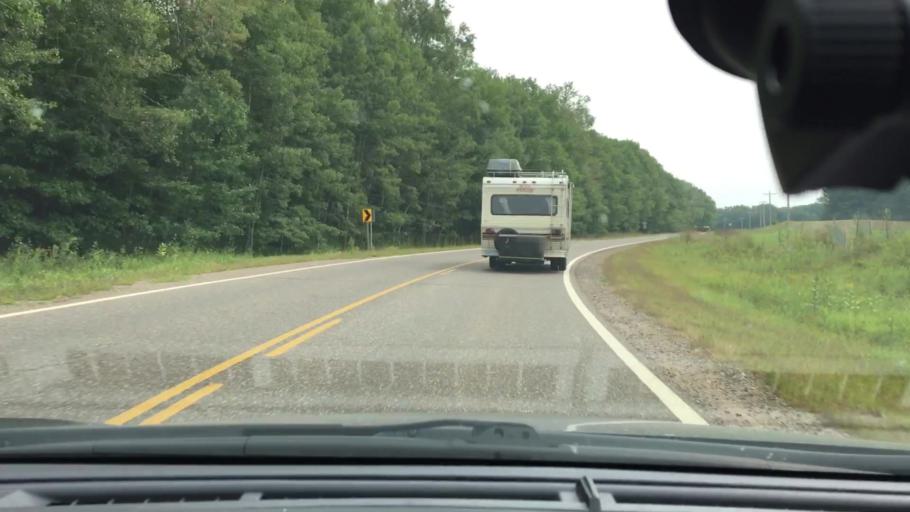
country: US
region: Minnesota
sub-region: Aitkin County
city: Aitkin
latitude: 46.4051
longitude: -93.7903
